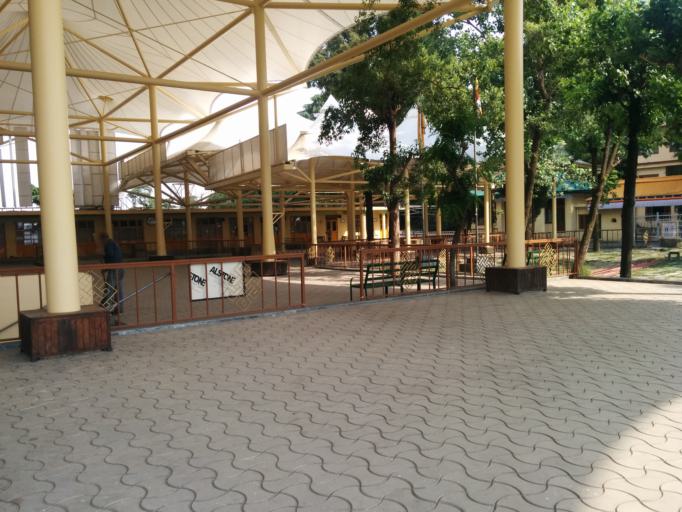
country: IN
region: Himachal Pradesh
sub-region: Kangra
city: Dharmsala
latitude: 32.2324
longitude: 76.3238
